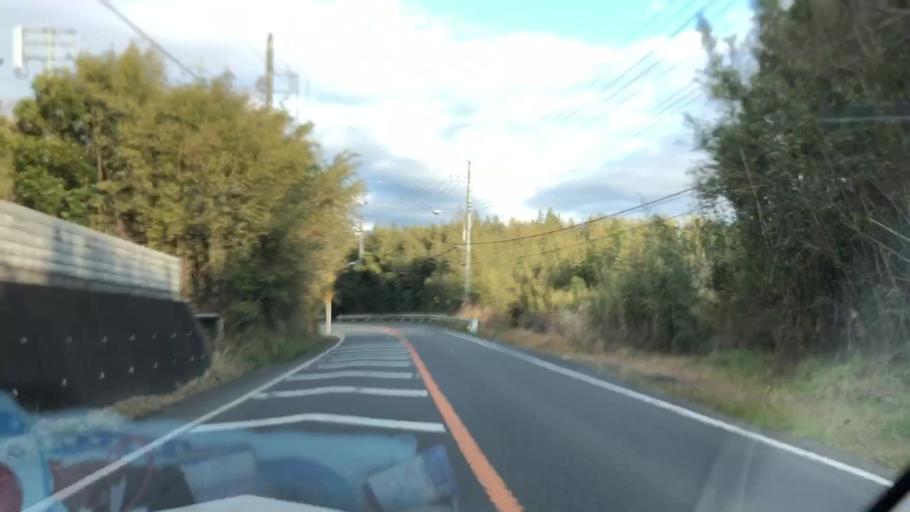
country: JP
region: Chiba
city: Tateyama
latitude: 34.9854
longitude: 139.9424
